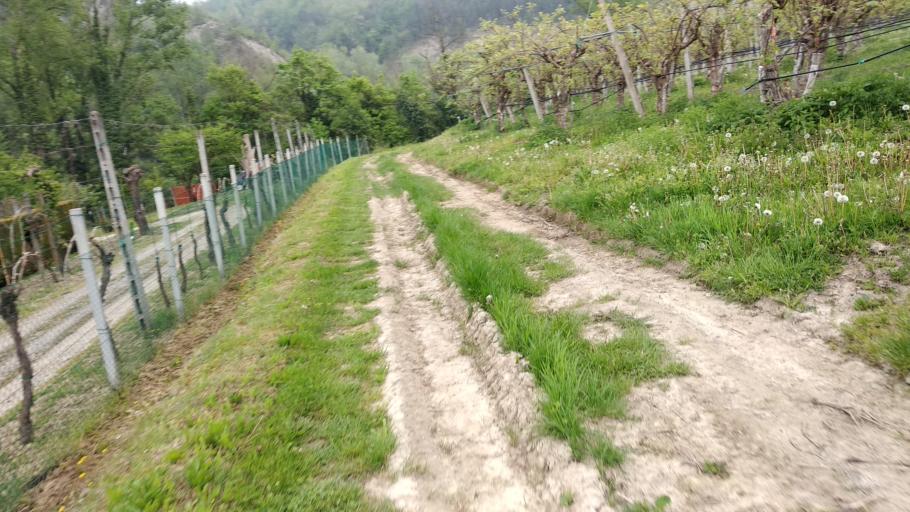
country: IT
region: Emilia-Romagna
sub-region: Forli-Cesena
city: Modigliana
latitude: 44.1432
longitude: 11.8013
